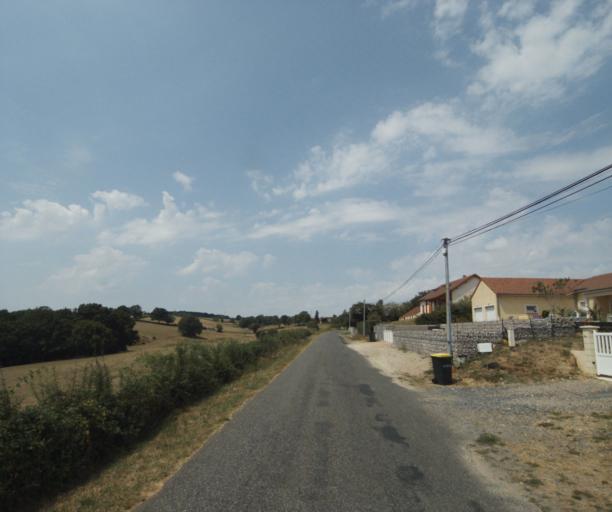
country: FR
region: Bourgogne
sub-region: Departement de Saone-et-Loire
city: Gueugnon
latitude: 46.6002
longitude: 4.0132
